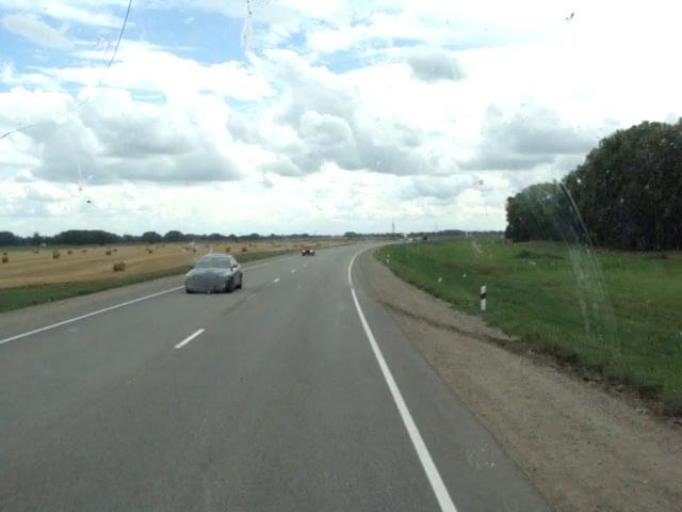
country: RU
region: Altai Krai
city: Shubenka
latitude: 52.6836
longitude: 85.0446
